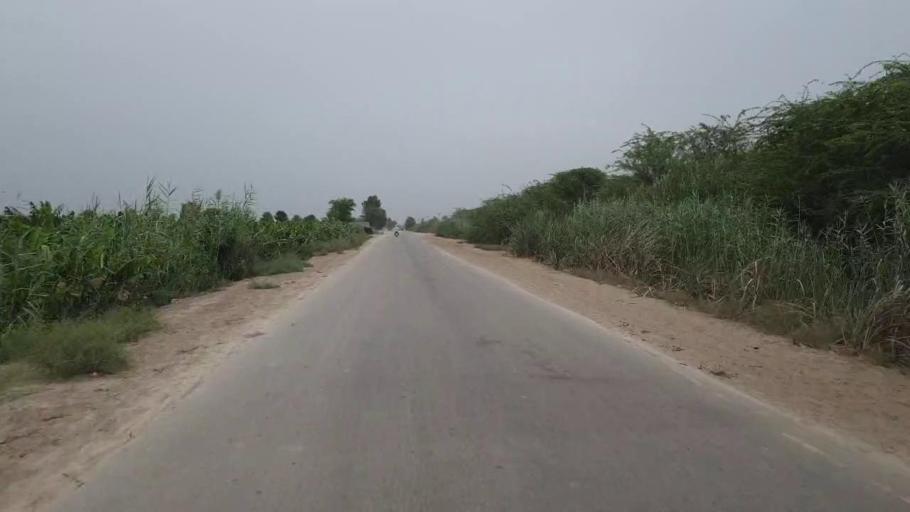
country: PK
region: Sindh
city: Bandhi
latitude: 26.5509
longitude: 68.2138
